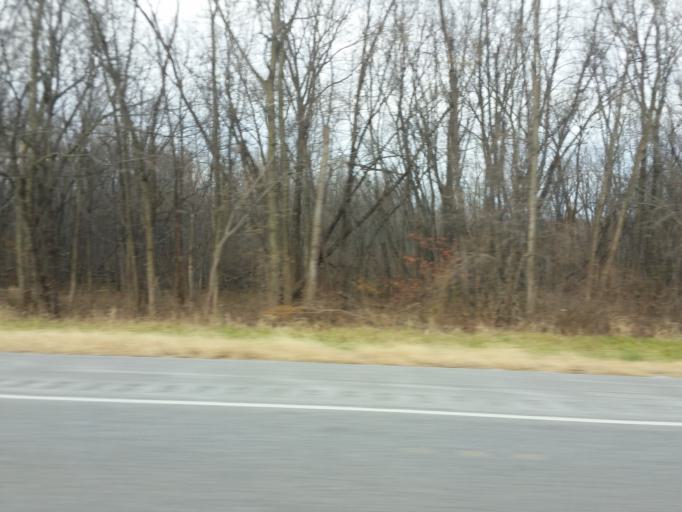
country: US
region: Illinois
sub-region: Rock Island County
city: Carbon Cliff
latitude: 41.4627
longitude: -90.3950
